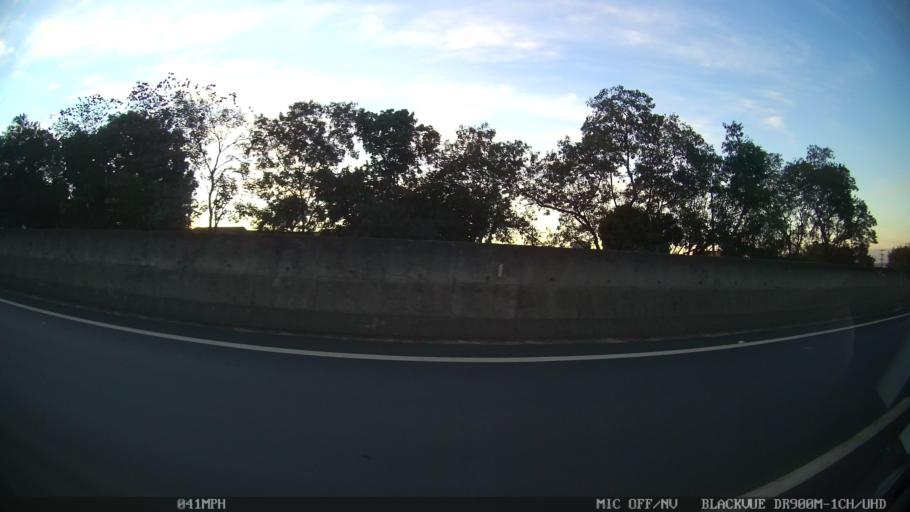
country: BR
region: Sao Paulo
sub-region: Catanduva
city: Catanduva
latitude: -21.1302
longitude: -49.0121
